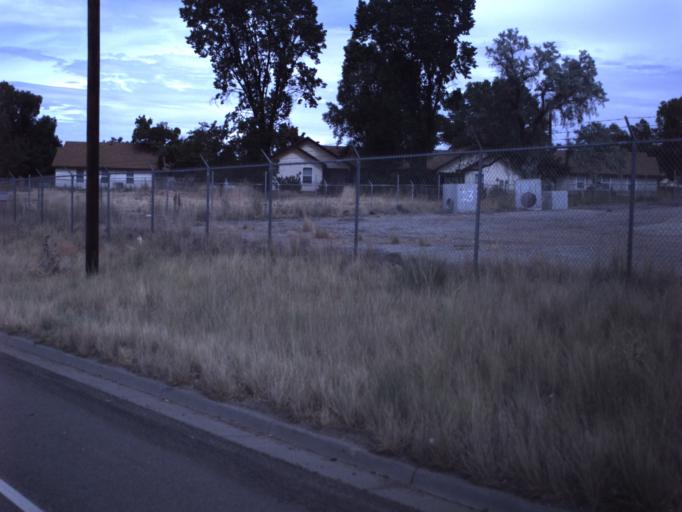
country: US
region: Utah
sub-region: Davis County
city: Hill Air Force Bace
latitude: 41.1036
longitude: -111.9899
